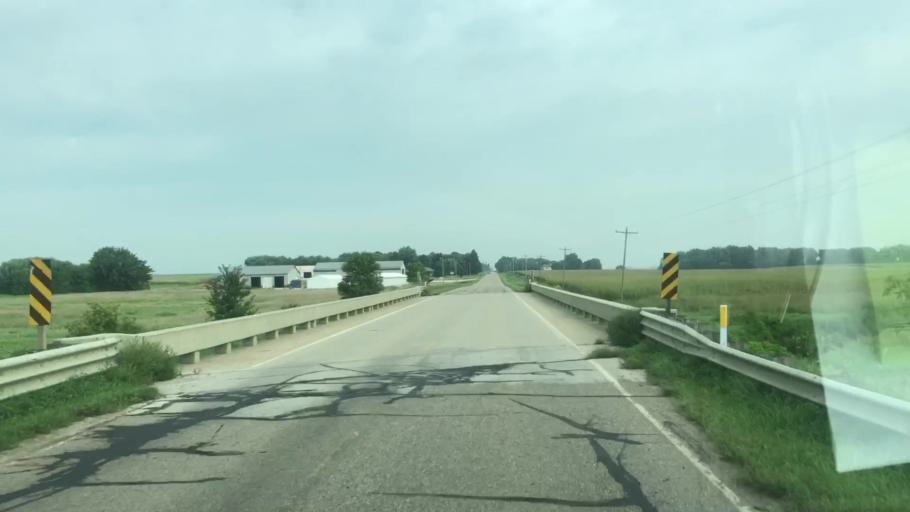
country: US
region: Iowa
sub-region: O'Brien County
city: Sheldon
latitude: 43.1911
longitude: -95.8622
